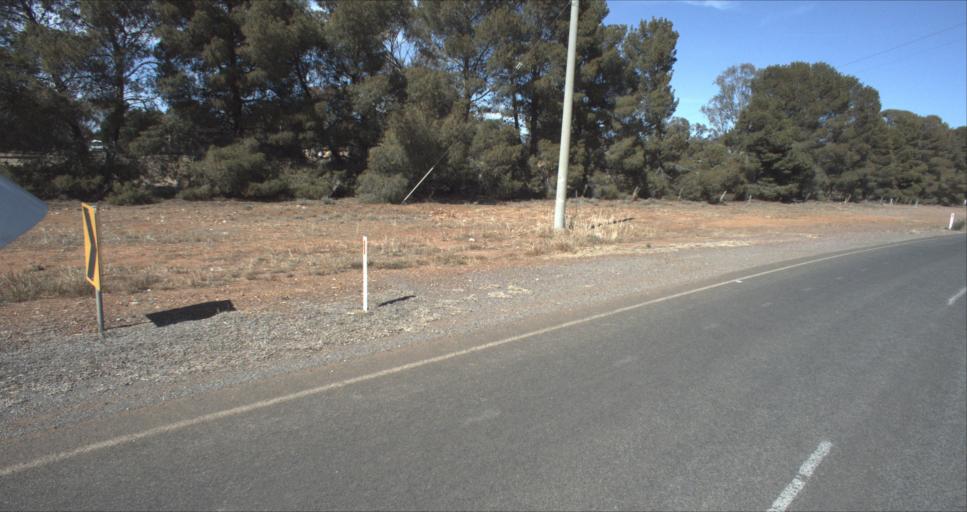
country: AU
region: New South Wales
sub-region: Leeton
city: Leeton
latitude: -34.5647
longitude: 146.4252
